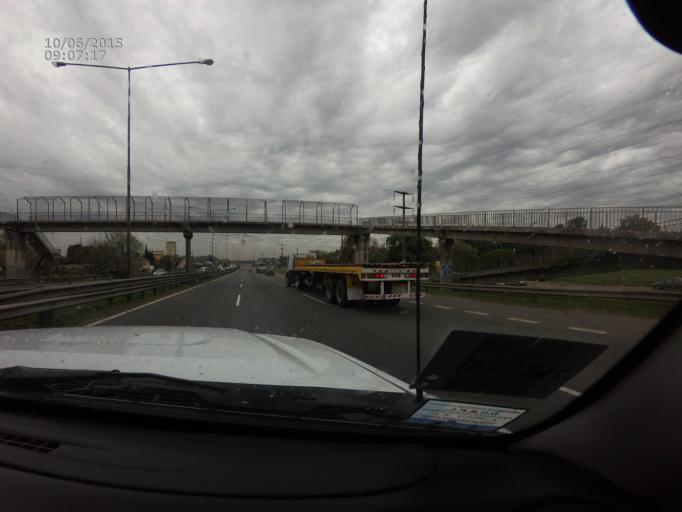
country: AR
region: Buenos Aires
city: Santa Catalina - Dique Lujan
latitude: -34.4050
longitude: -58.7325
